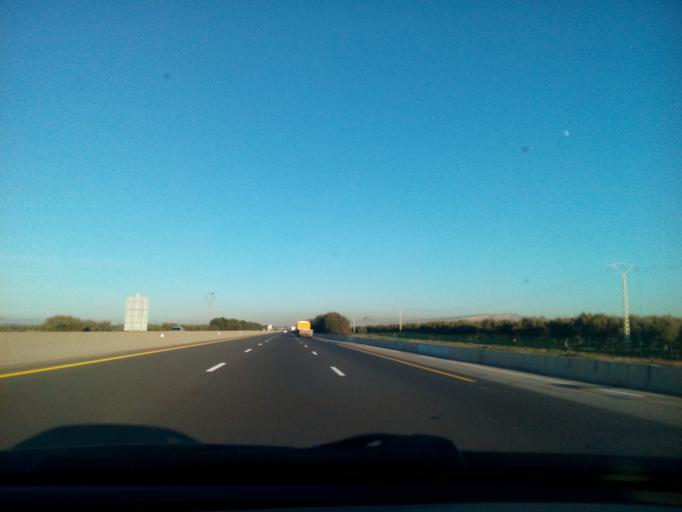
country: DZ
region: Relizane
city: Djidiouia
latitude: 35.9228
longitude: 0.7791
